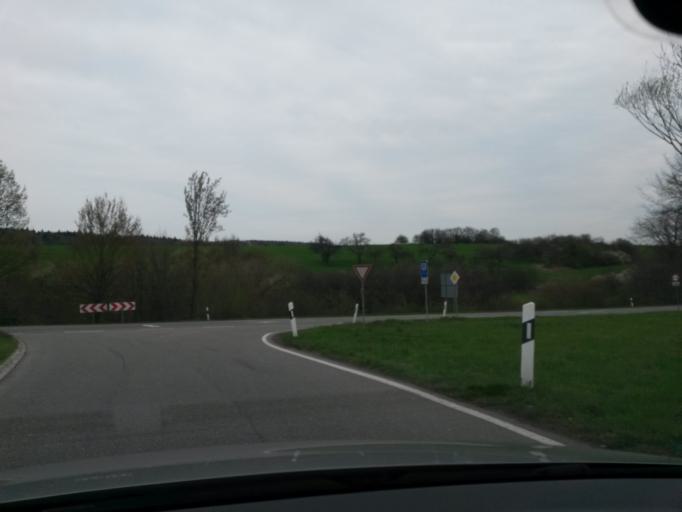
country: DE
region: Baden-Wuerttemberg
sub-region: Karlsruhe Region
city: Neuenburg
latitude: 48.8959
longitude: 8.5504
